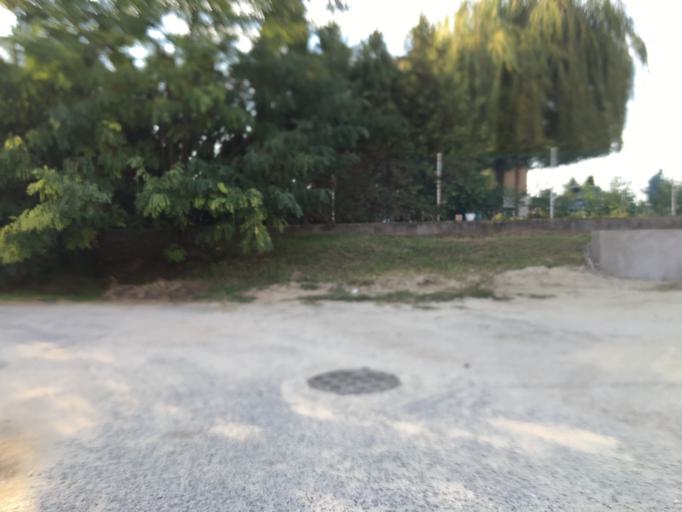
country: HU
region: Pest
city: Szigetszentmiklos
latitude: 47.3475
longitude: 19.0257
